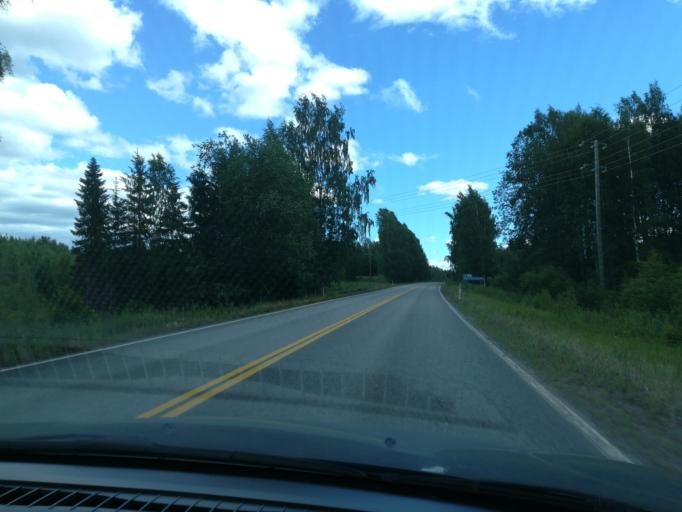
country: FI
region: Southern Savonia
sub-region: Mikkeli
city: Hirvensalmi
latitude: 61.6706
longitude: 26.8831
